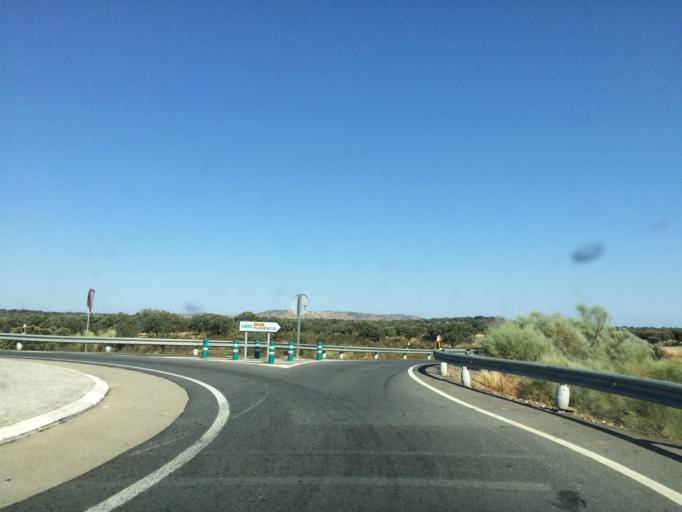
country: ES
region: Extremadura
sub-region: Provincia de Caceres
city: Malpartida de Plasencia
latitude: 39.9734
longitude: -6.0941
